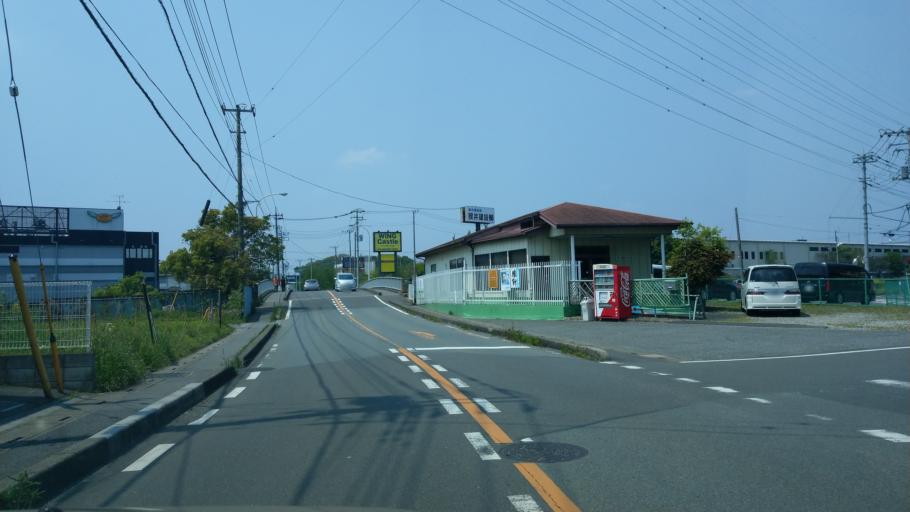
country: JP
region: Saitama
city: Yono
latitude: 35.9150
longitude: 139.5978
